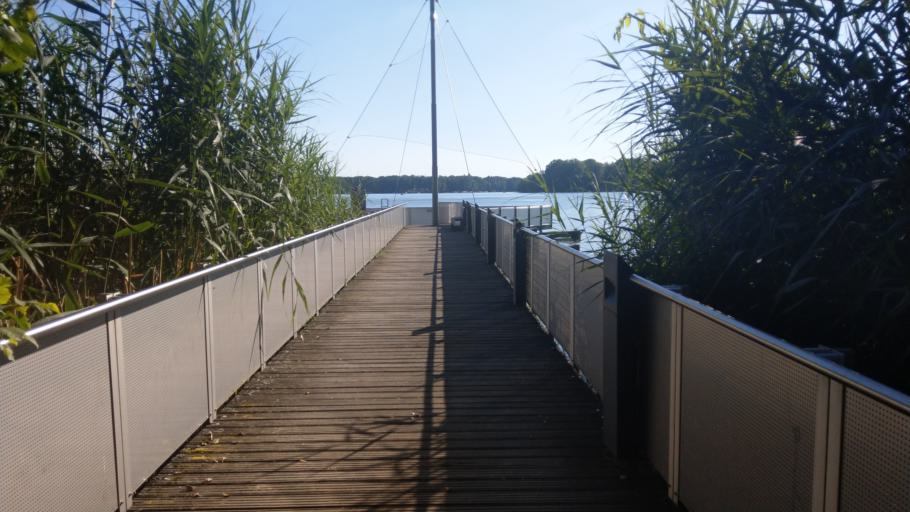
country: DE
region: Brandenburg
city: Teupitz
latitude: 52.1370
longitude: 13.6073
